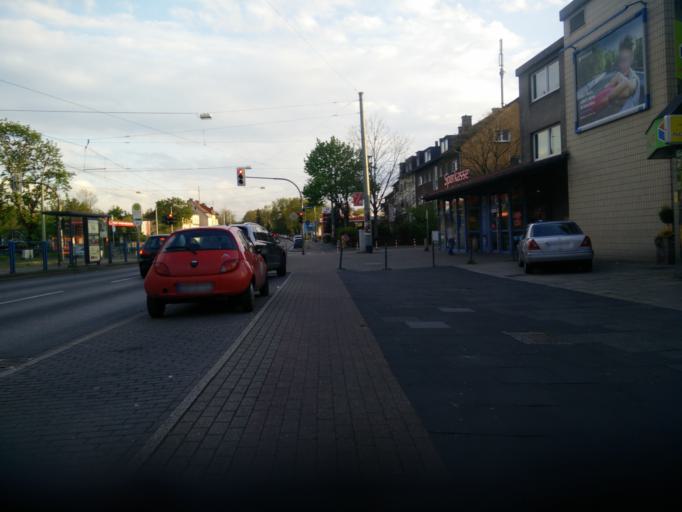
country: DE
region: North Rhine-Westphalia
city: Bochum-Hordel
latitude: 51.5026
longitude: 7.1887
